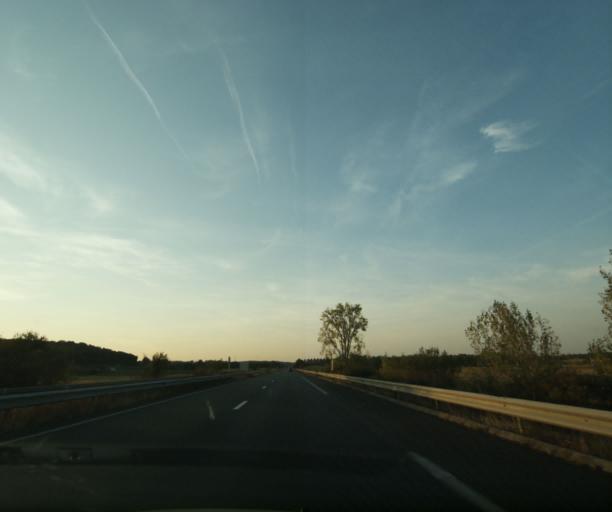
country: FR
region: Aquitaine
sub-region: Departement du Lot-et-Garonne
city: Damazan
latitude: 44.2705
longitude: 0.2766
